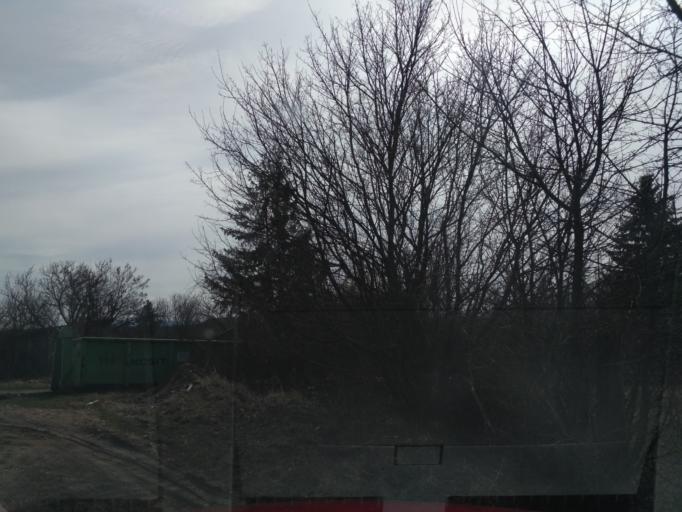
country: SK
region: Kosicky
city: Kosice
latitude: 48.7087
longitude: 21.2880
